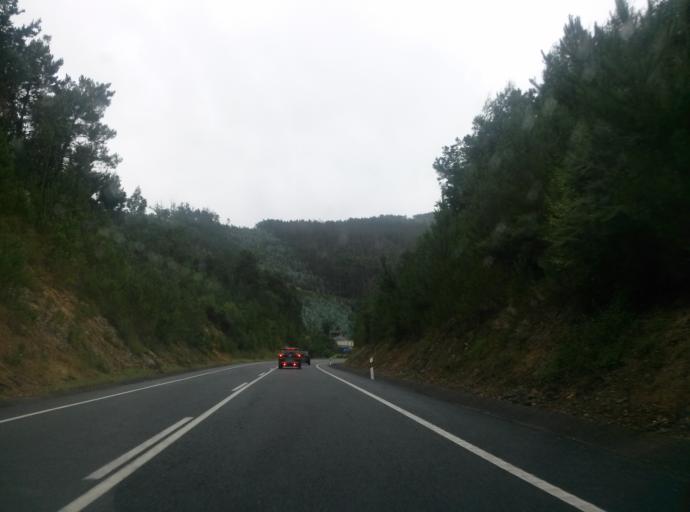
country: ES
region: Galicia
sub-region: Provincia de Lugo
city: Viveiro
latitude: 43.5902
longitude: -7.6281
